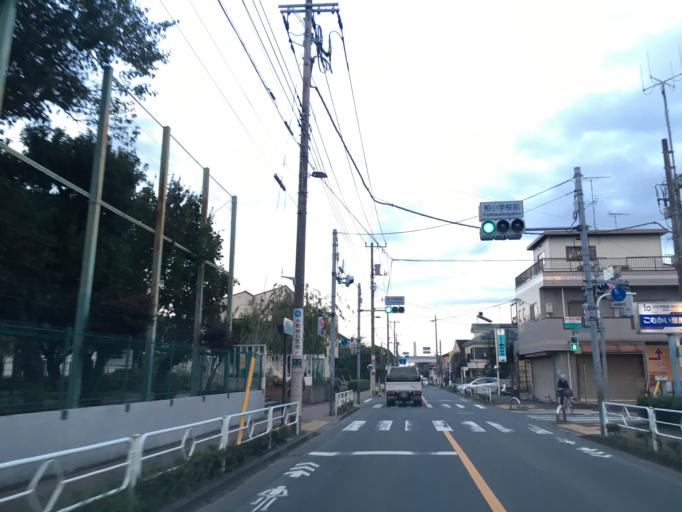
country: JP
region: Tokyo
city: Hino
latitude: 35.7266
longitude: 139.4150
